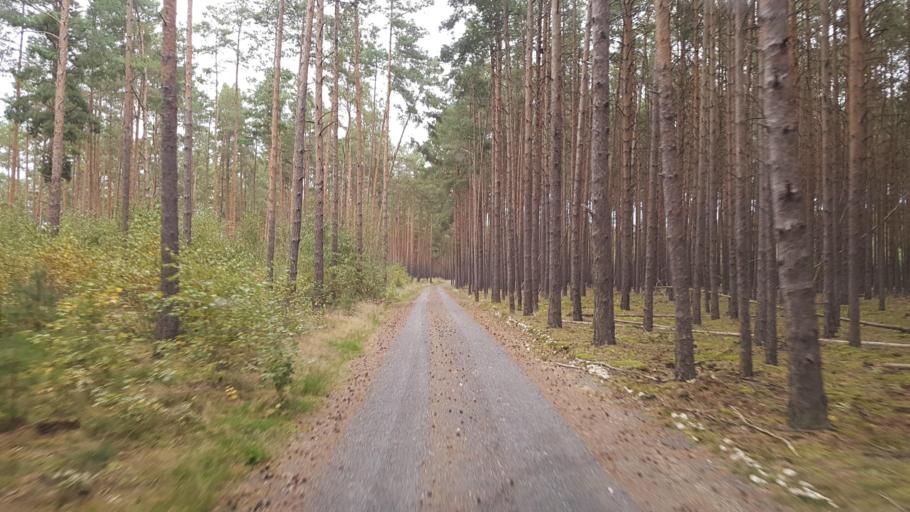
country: DE
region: Brandenburg
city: Sonnewalde
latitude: 51.7227
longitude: 13.6654
